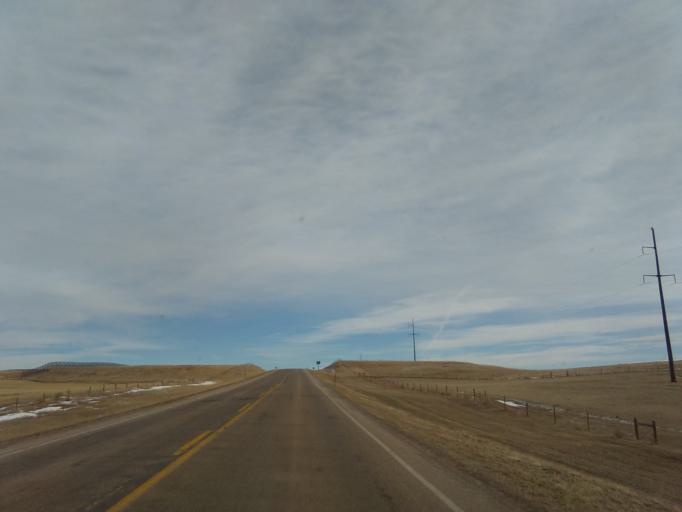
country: US
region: Wyoming
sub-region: Laramie County
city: Ranchettes
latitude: 41.3823
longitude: -104.5230
